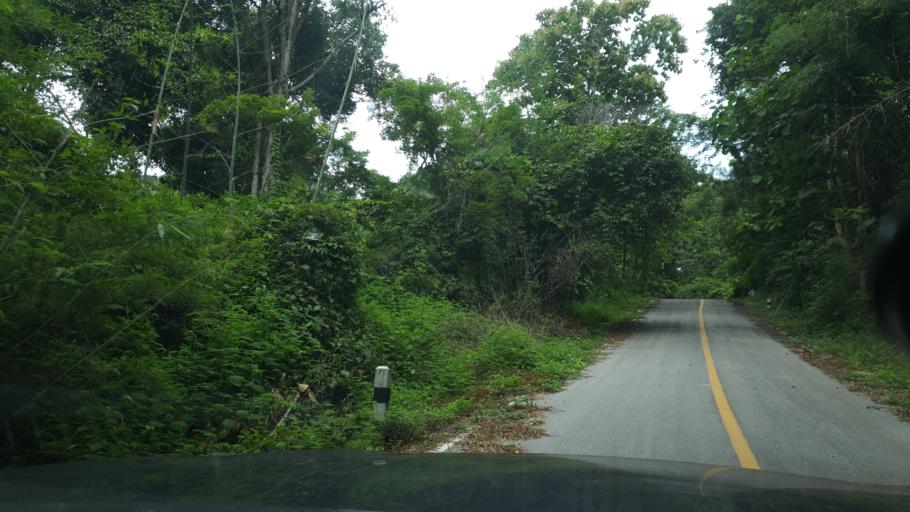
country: TH
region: Lamphun
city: Mae Tha
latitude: 18.4909
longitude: 99.2672
